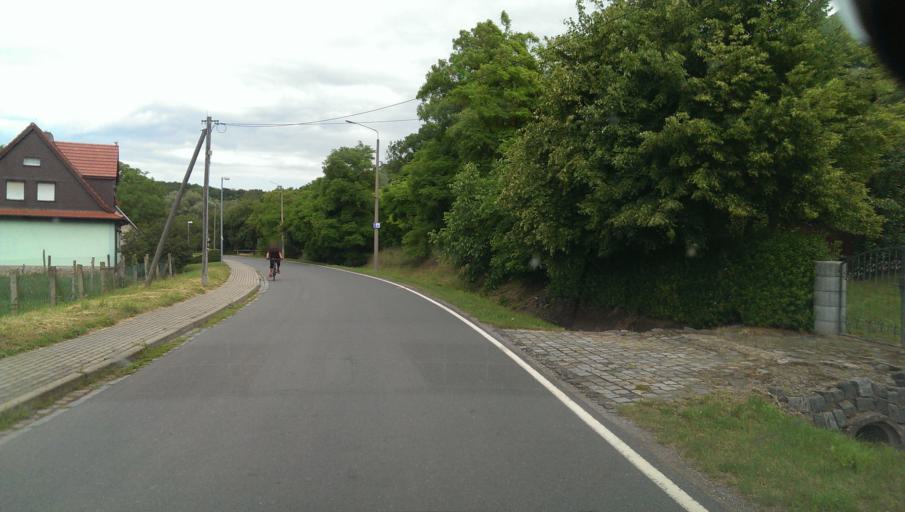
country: DE
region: Saxony-Anhalt
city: Hohnstedt
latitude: 51.4922
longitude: 11.7019
